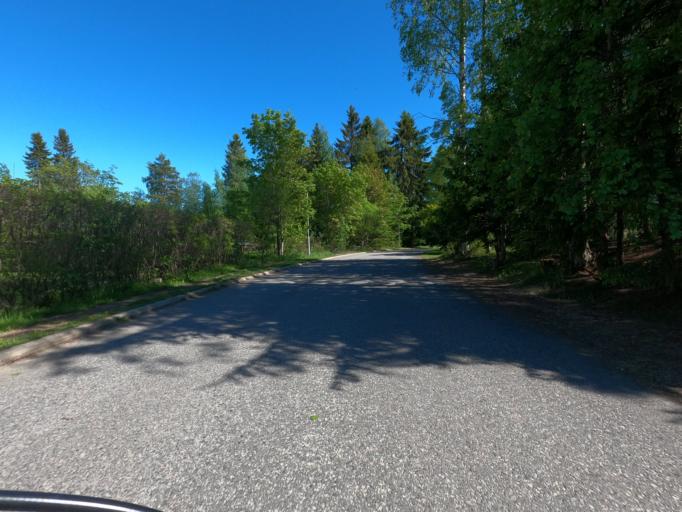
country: FI
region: North Karelia
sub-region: Joensuu
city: Joensuu
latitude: 62.5915
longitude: 29.7979
